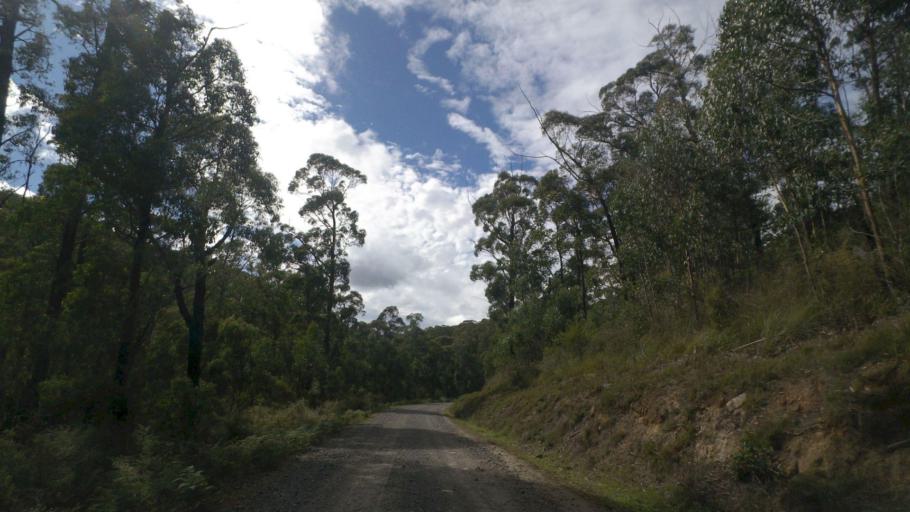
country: AU
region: Victoria
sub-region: Cardinia
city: Bunyip
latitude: -37.9829
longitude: 145.8157
